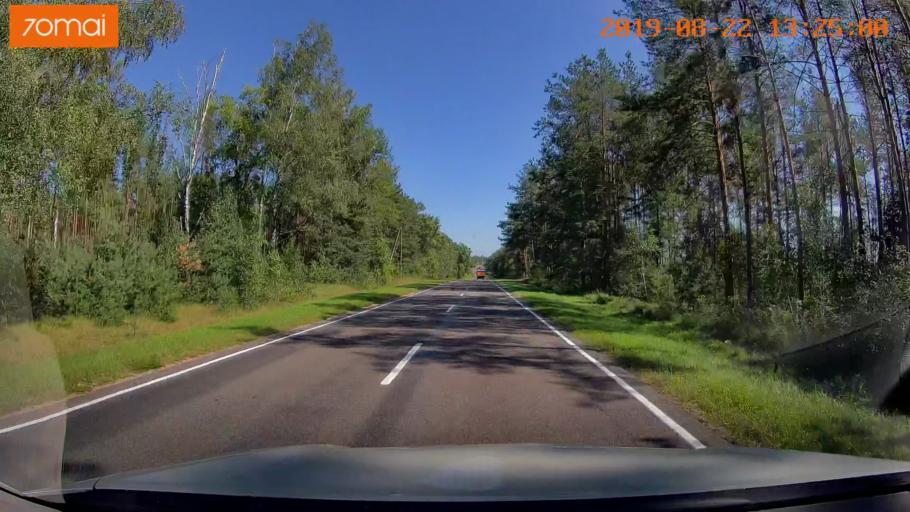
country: BY
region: Minsk
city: Staryya Darohi
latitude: 53.2115
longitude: 28.0351
